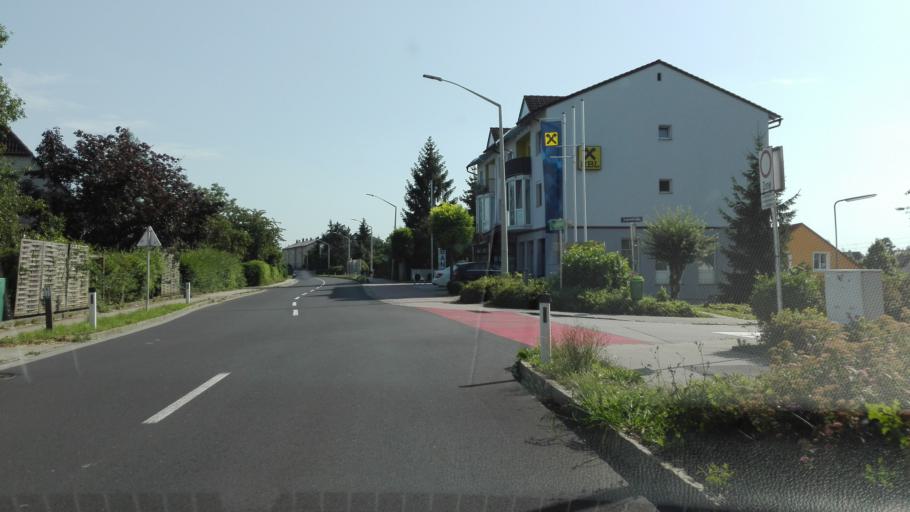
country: AT
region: Upper Austria
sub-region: Politischer Bezirk Linz-Land
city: Leonding
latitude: 48.2509
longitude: 14.2596
